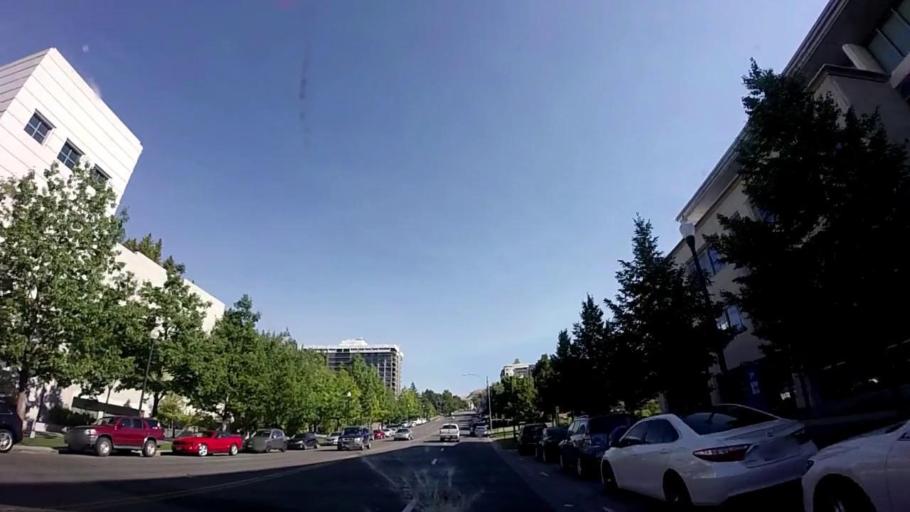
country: US
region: Utah
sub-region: Salt Lake County
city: Salt Lake City
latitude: 40.7720
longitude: -111.8910
